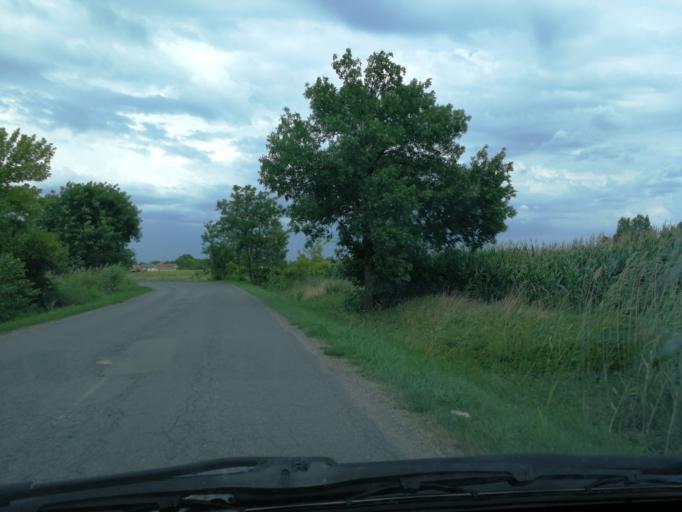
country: HU
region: Bacs-Kiskun
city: Kalocsa
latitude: 46.4931
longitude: 19.0582
